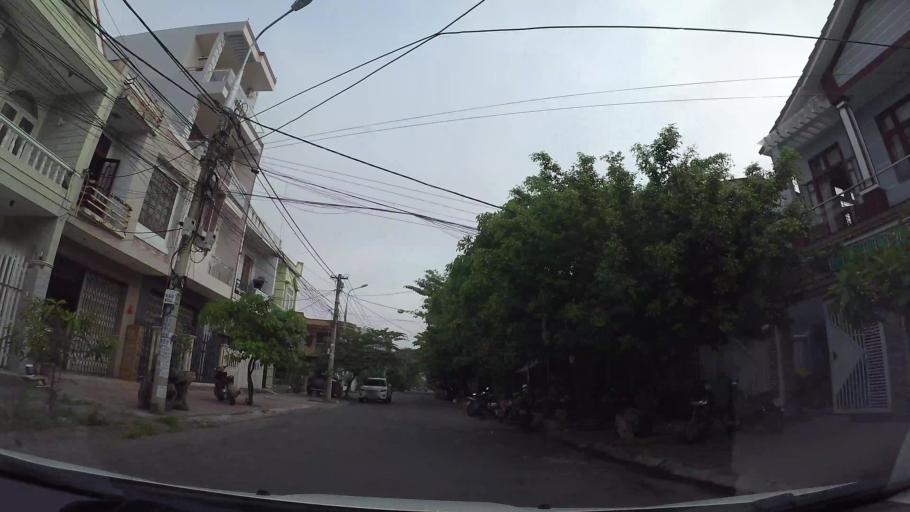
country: VN
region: Da Nang
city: Son Tra
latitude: 16.0918
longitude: 108.2480
